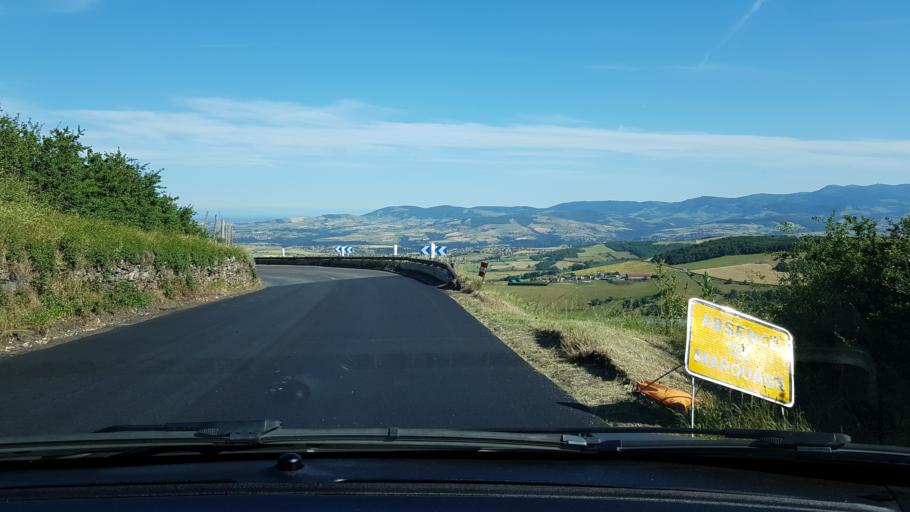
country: FR
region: Rhone-Alpes
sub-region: Departement du Rhone
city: Saint-Didier-sous-Riverie
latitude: 45.5952
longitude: 4.5887
